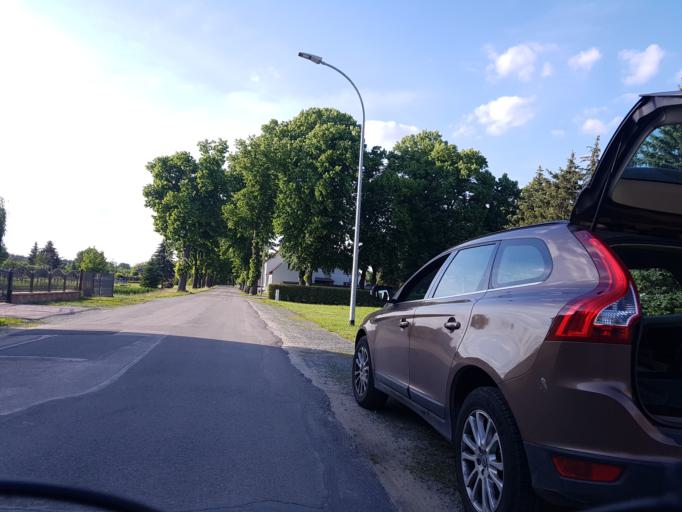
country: DE
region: Brandenburg
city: Elsterwerda
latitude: 51.4457
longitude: 13.5301
